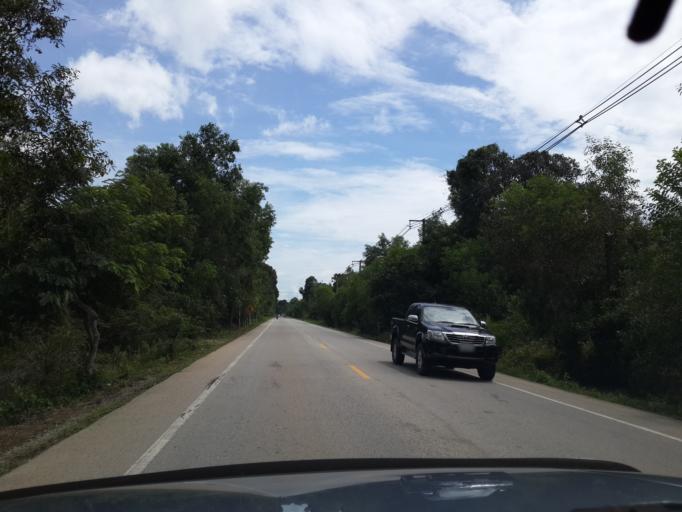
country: TH
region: Narathiwat
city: Narathiwat
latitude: 6.4478
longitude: 101.7940
